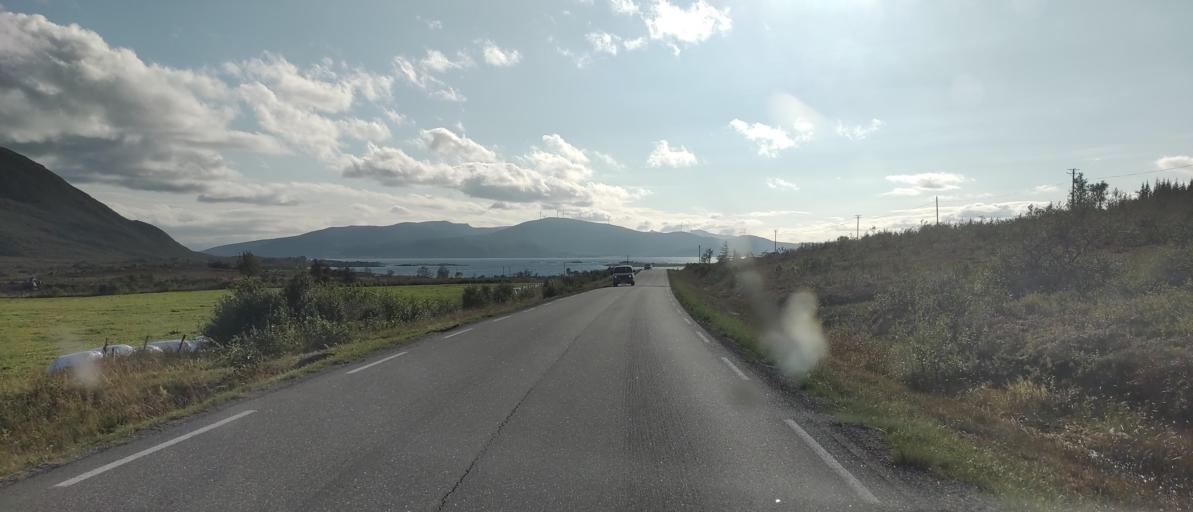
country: NO
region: Nordland
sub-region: Sortland
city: Sortland
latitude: 68.7893
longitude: 15.4987
